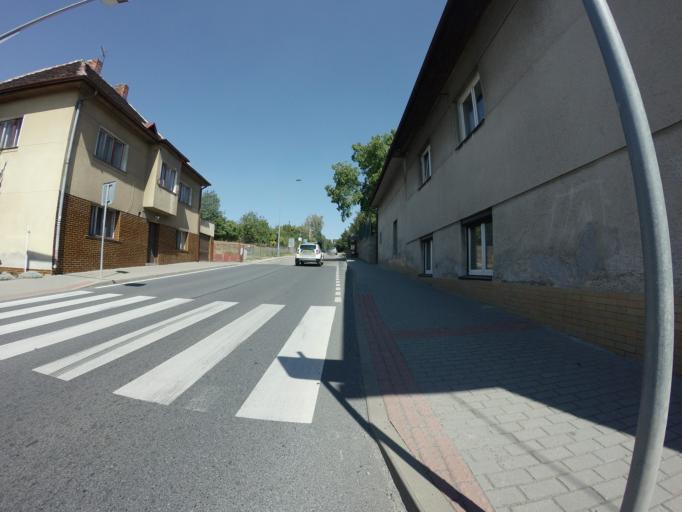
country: CZ
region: Central Bohemia
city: Jilove u Prahy
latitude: 49.8986
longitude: 14.4939
